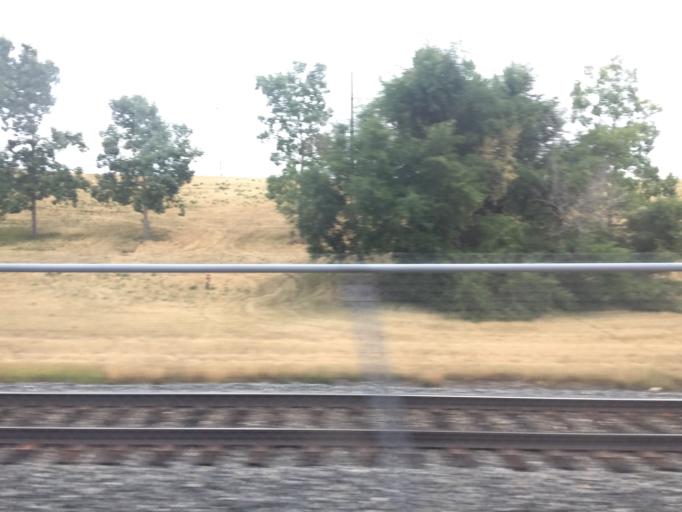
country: CA
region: Alberta
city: Calgary
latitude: 50.9483
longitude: -114.0725
